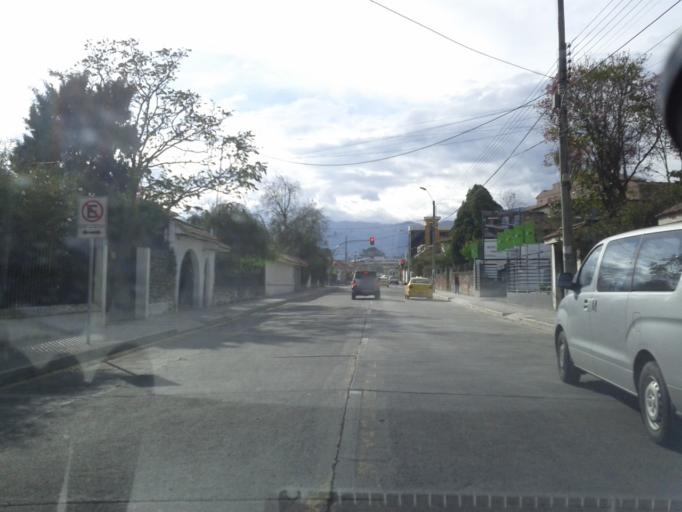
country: EC
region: Azuay
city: Cuenca
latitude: -2.9038
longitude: -79.0118
